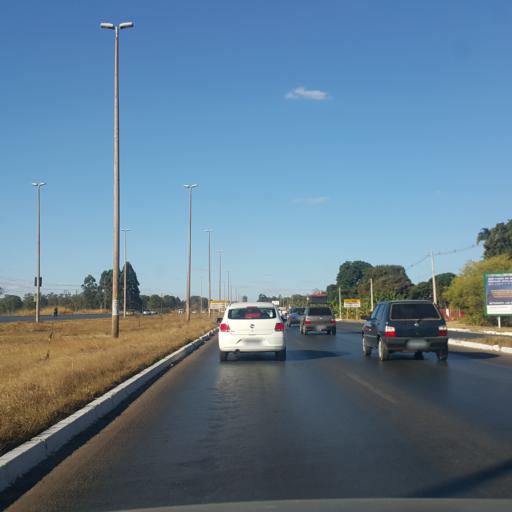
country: BR
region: Federal District
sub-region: Brasilia
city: Brasilia
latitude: -15.7970
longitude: -48.0694
